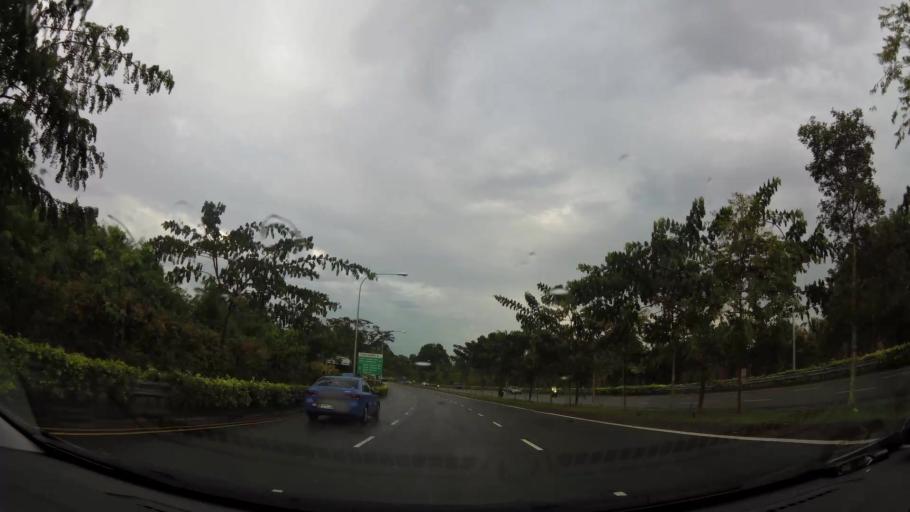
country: MY
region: Johor
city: Kampung Pasir Gudang Baru
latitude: 1.4046
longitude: 103.8687
